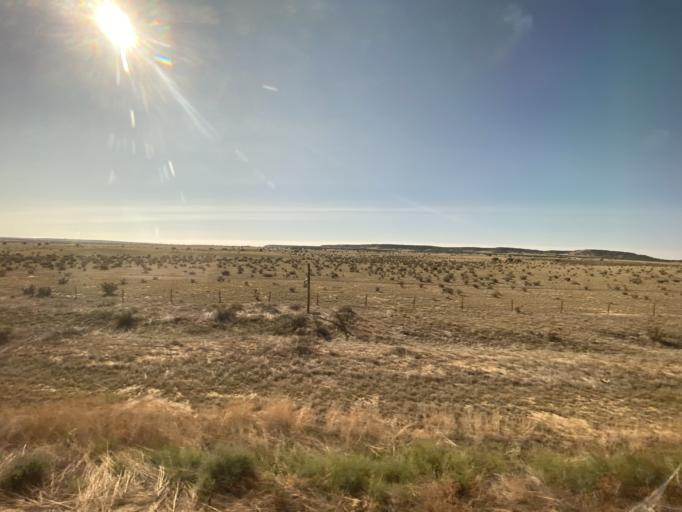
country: US
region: Colorado
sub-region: Otero County
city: Fowler
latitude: 37.5638
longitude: -104.0821
